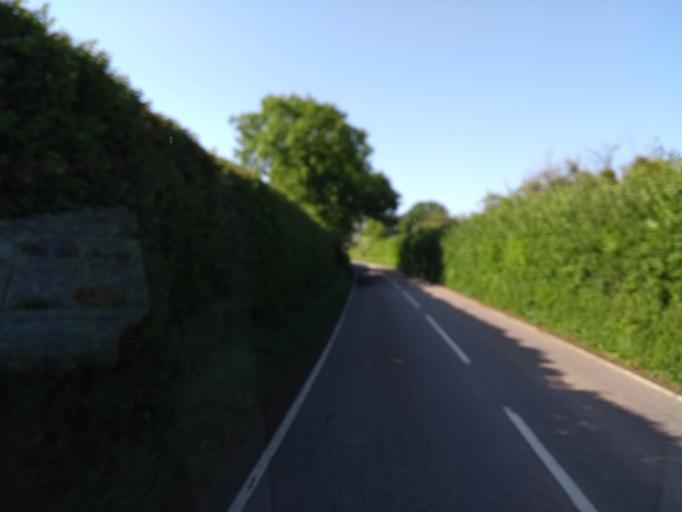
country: GB
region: England
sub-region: Somerset
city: Taunton
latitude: 50.9831
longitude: -3.0887
